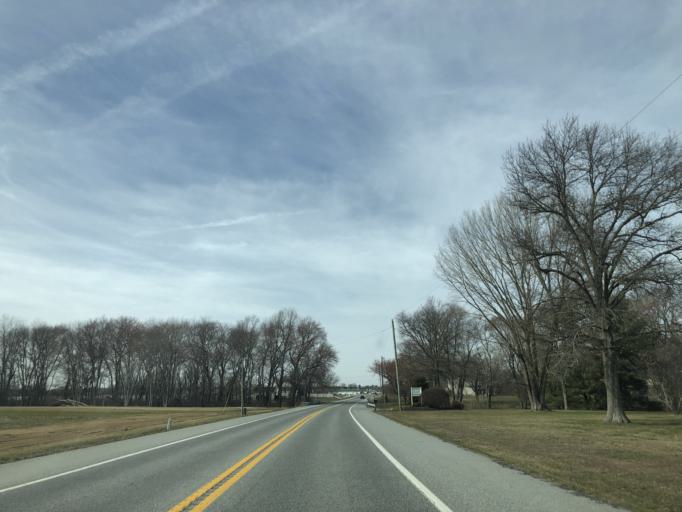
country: US
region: Delaware
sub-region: Kent County
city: Smyrna
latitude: 39.2836
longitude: -75.5755
